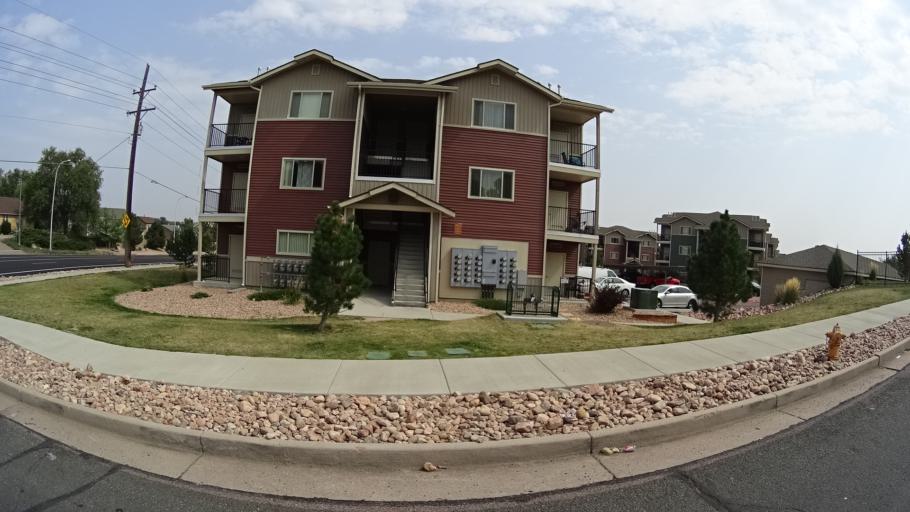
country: US
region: Colorado
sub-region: El Paso County
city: Cimarron Hills
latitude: 38.8251
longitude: -104.7451
